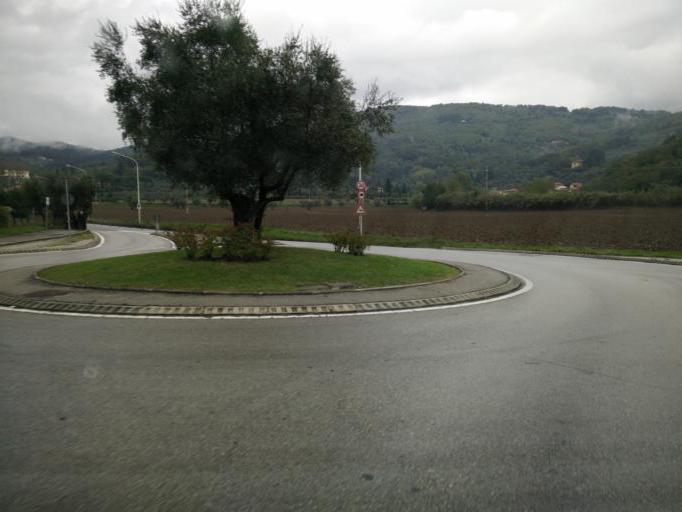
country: IT
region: Tuscany
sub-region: Provincia di Prato
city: Prato
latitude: 43.9138
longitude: 11.0945
